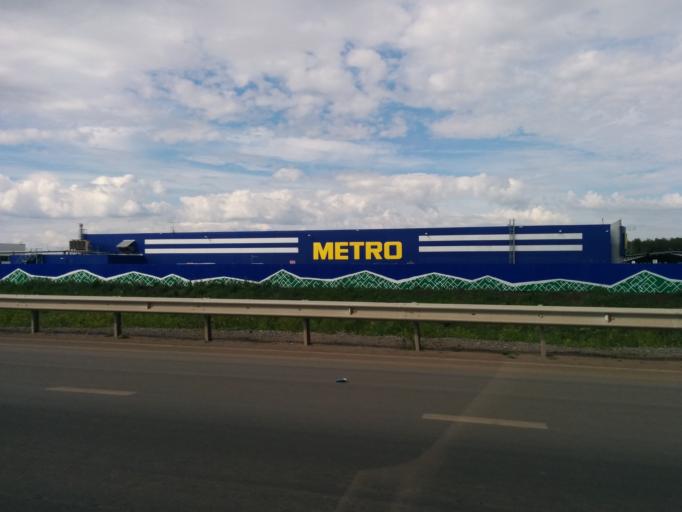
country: RU
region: Bashkortostan
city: Ufa
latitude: 54.6688
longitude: 55.9333
